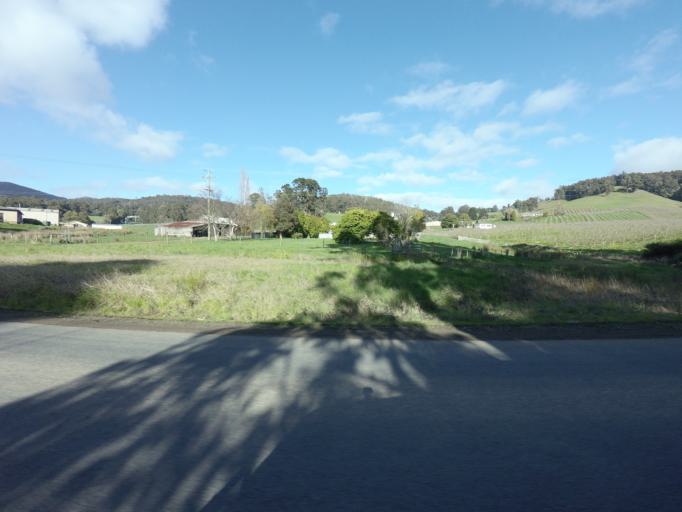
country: AU
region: Tasmania
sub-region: Huon Valley
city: Geeveston
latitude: -43.1896
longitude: 146.9595
